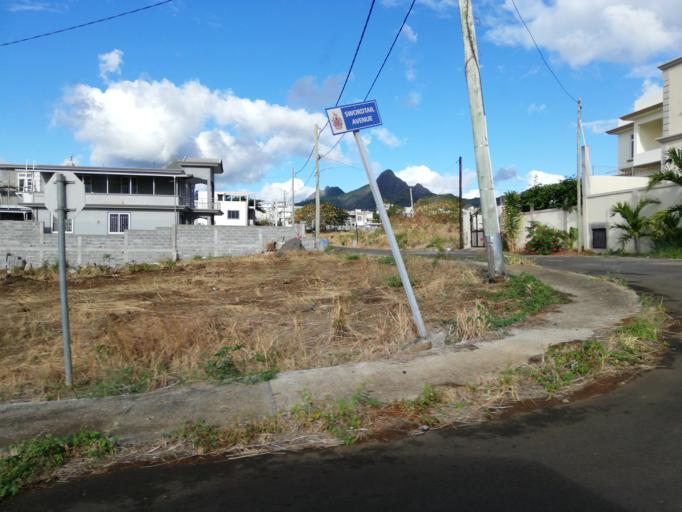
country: MU
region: Black River
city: Petite Riviere
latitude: -20.2000
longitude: 57.4624
